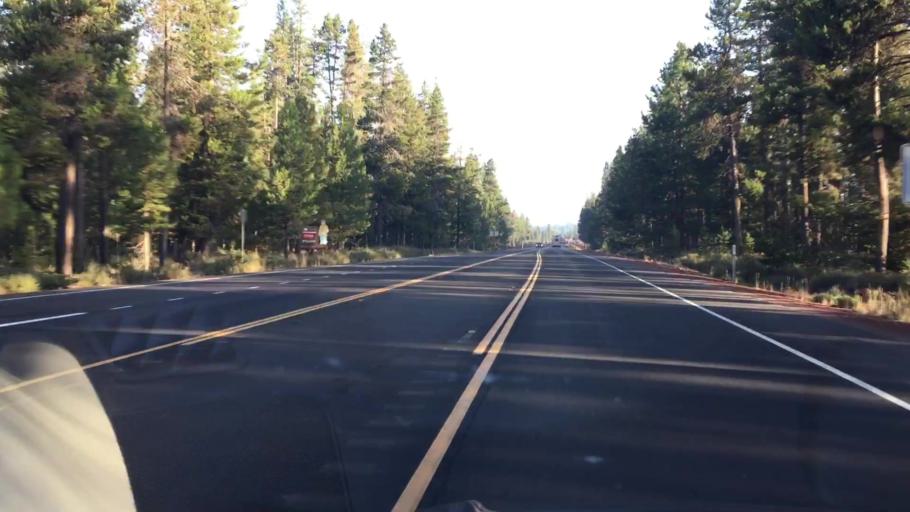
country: US
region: Oregon
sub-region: Deschutes County
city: La Pine
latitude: 43.2263
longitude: -121.7879
